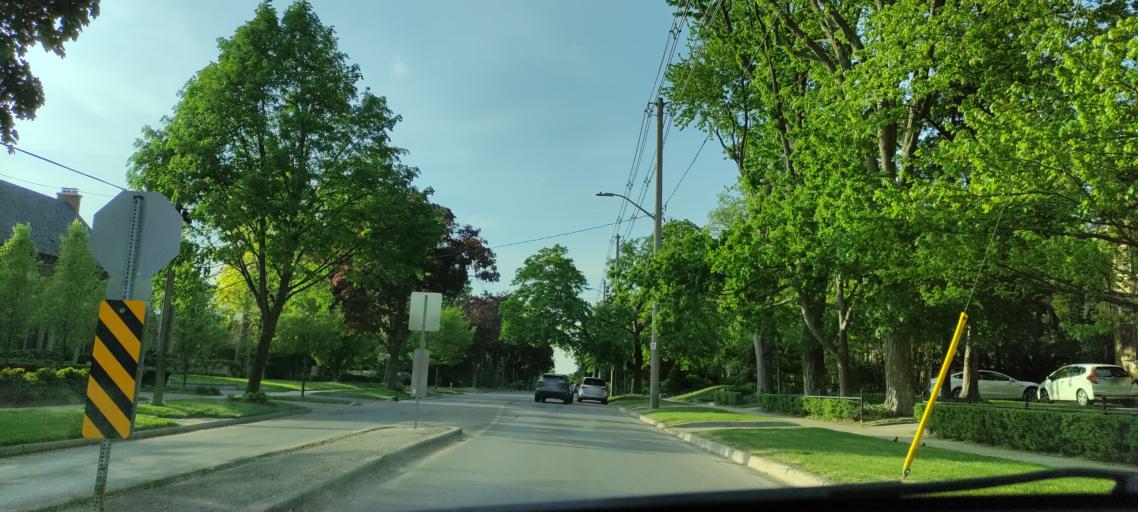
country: CA
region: Ontario
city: London
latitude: 42.9991
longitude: -81.2575
